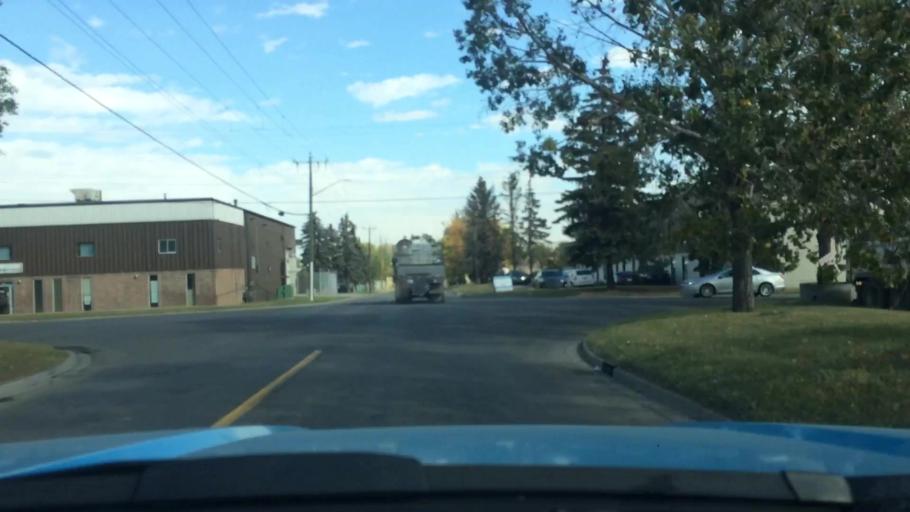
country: CA
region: Alberta
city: Calgary
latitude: 50.9962
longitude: -113.9765
